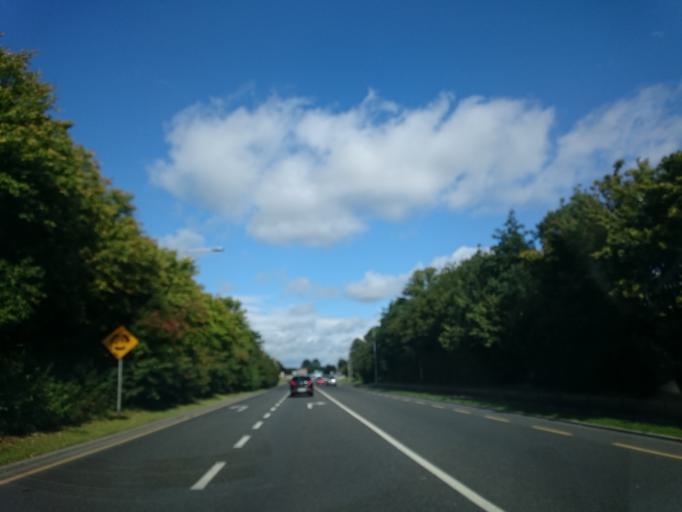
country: IE
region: Leinster
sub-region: Kilkenny
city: Kilkenny
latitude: 52.6413
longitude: -7.2614
